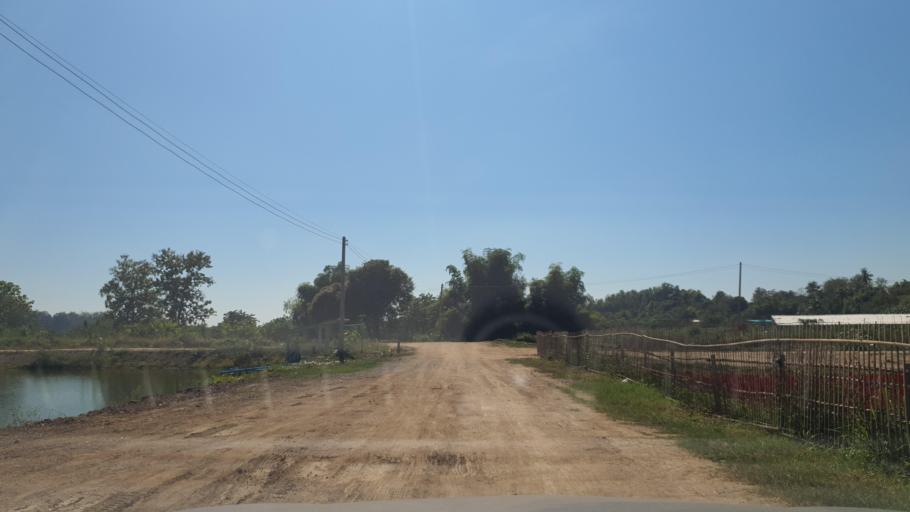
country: TH
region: Chiang Mai
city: Mae Wang
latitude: 18.6838
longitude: 98.8108
